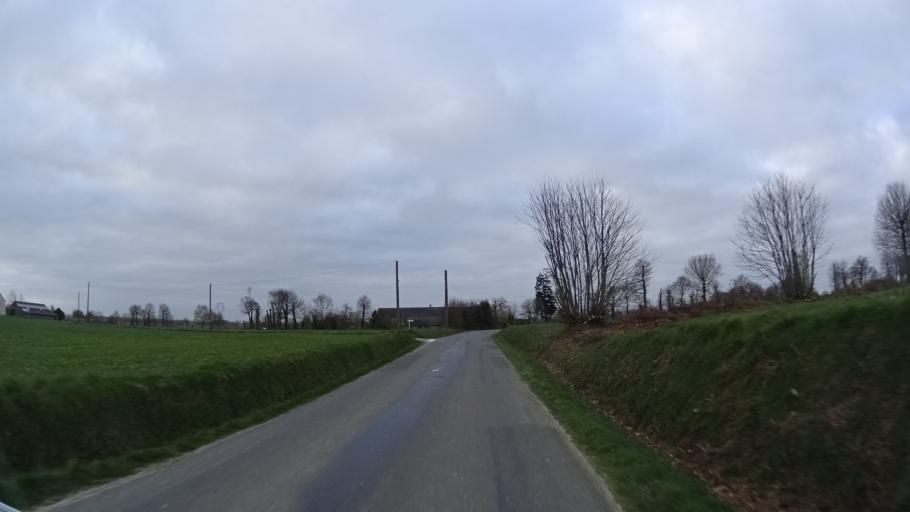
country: FR
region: Brittany
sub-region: Departement d'Ille-et-Vilaine
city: Geveze
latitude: 48.2083
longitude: -1.8275
